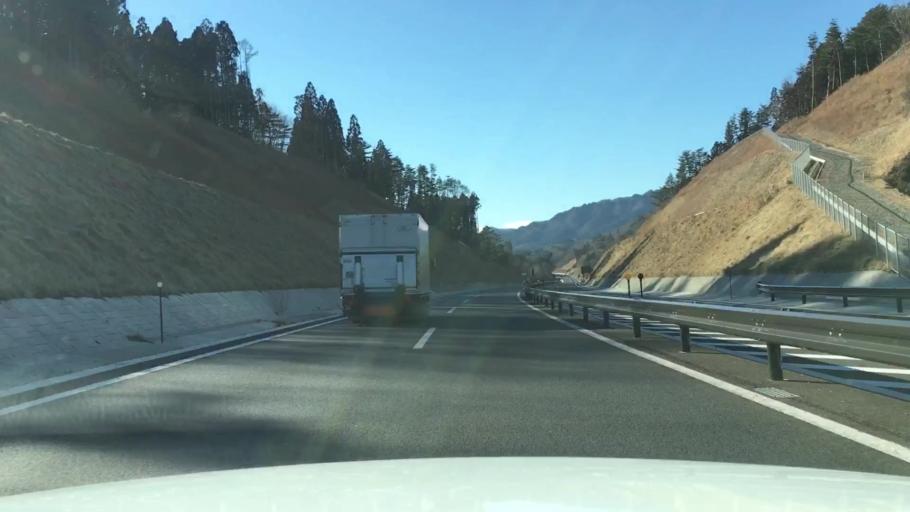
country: JP
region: Iwate
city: Miyako
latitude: 39.5890
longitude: 141.9394
